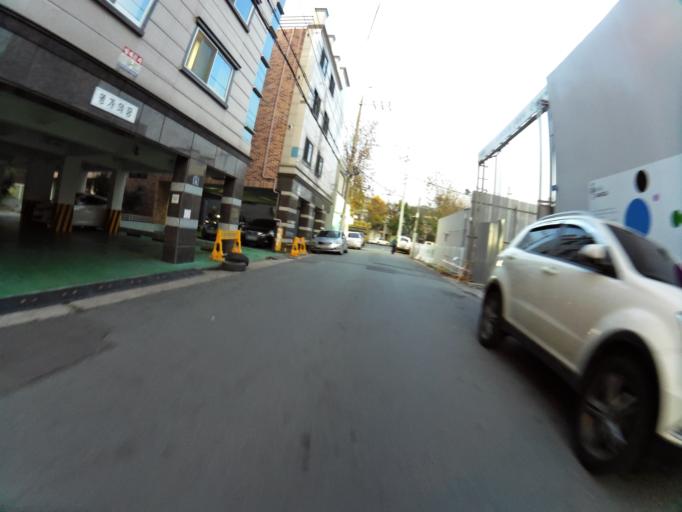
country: KR
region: Daegu
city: Daegu
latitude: 35.8603
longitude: 128.6443
